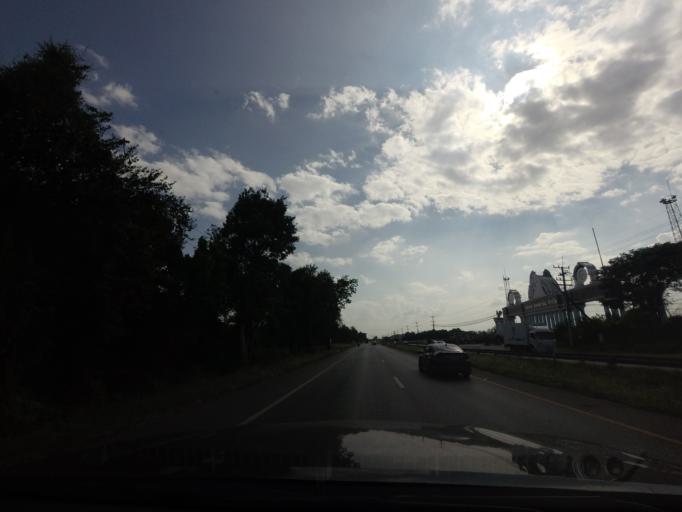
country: TH
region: Lop Buri
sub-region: Amphoe Tha Luang
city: Tha Luang
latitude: 15.0956
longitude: 101.0164
